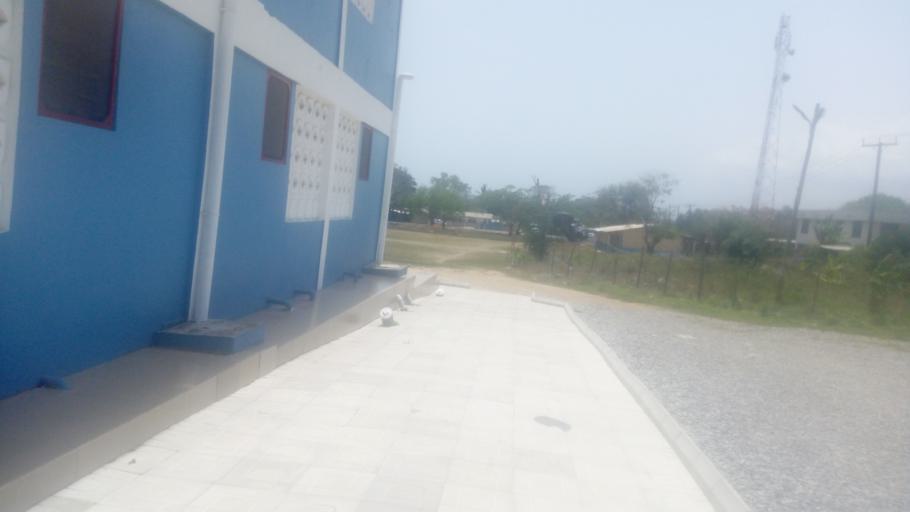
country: GH
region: Central
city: Winneba
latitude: 5.3604
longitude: -0.6320
